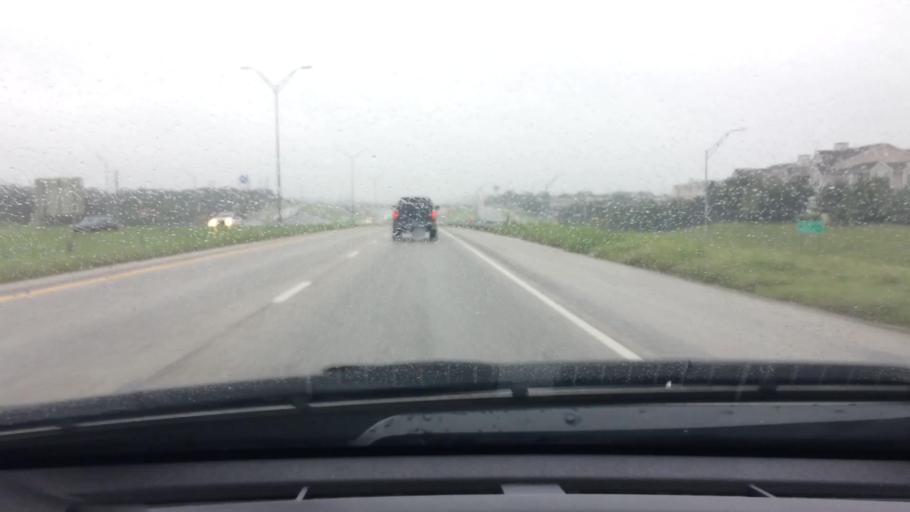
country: US
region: Texas
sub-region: Bexar County
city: Leon Valley
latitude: 29.4580
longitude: -98.6890
